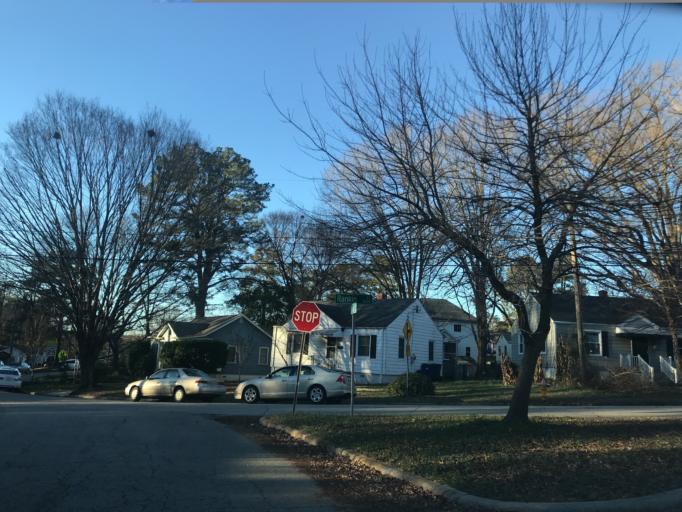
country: US
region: North Carolina
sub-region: Wake County
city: Raleigh
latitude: 35.7969
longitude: -78.6207
